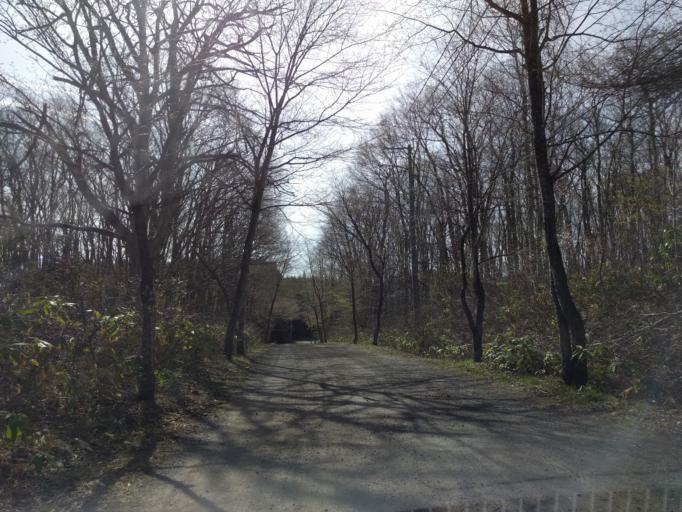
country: JP
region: Fukushima
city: Inawashiro
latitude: 37.5290
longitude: 140.0321
